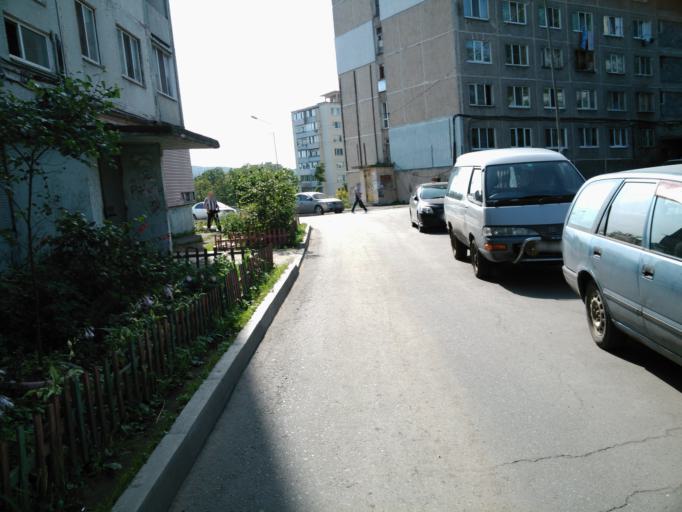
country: RU
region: Primorskiy
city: Vladivostok
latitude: 43.0931
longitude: 131.9718
